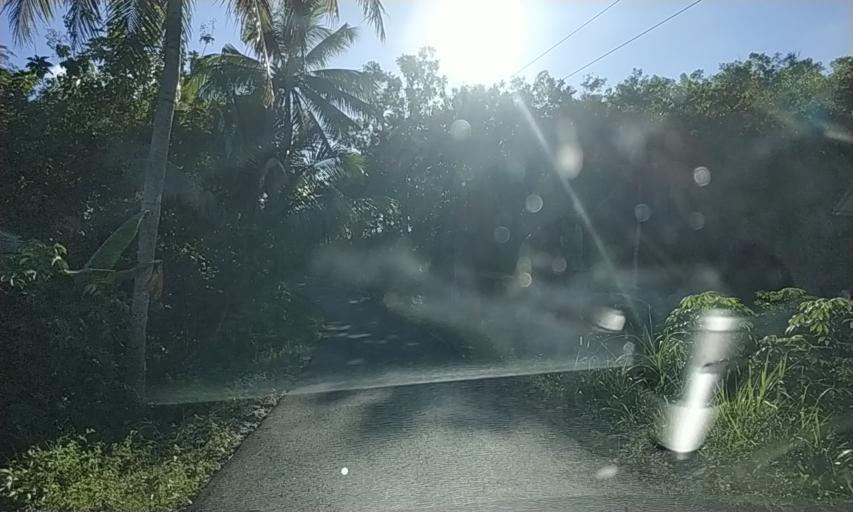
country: ID
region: East Java
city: Krajan
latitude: -8.1279
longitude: 110.9017
